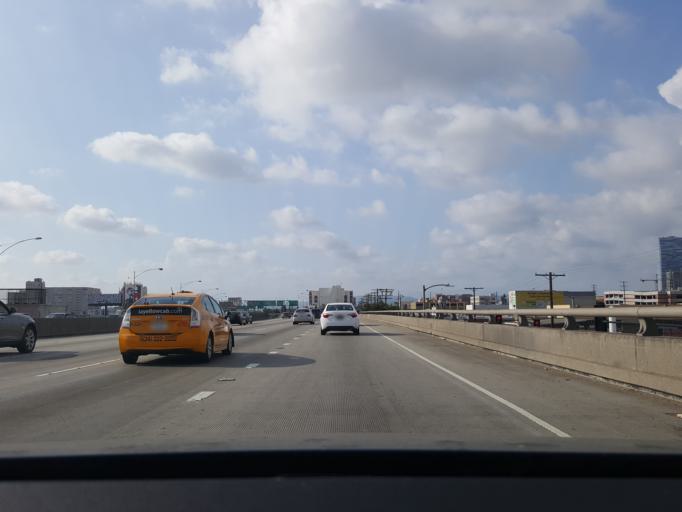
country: US
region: California
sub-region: Los Angeles County
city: Los Angeles
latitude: 34.0294
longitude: -118.2554
